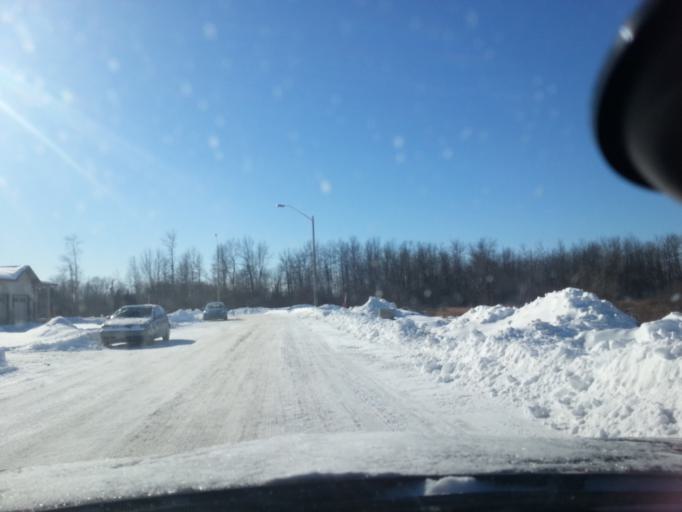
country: CA
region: Ontario
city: Carleton Place
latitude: 45.2365
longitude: -76.1881
